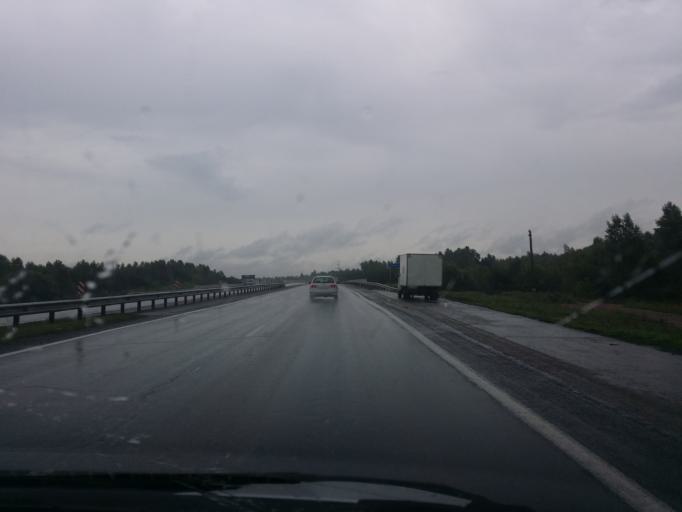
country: RU
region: Altai Krai
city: Sannikovo
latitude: 53.3272
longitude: 83.9150
